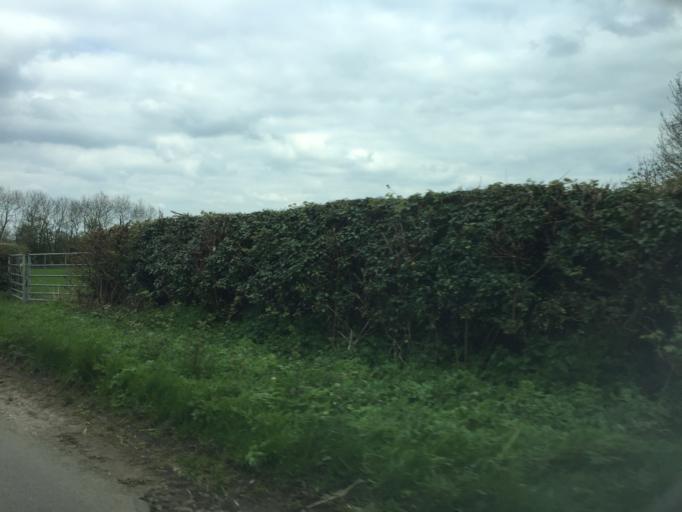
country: GB
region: England
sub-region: Oxfordshire
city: Bicester
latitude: 51.9360
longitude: -1.1386
